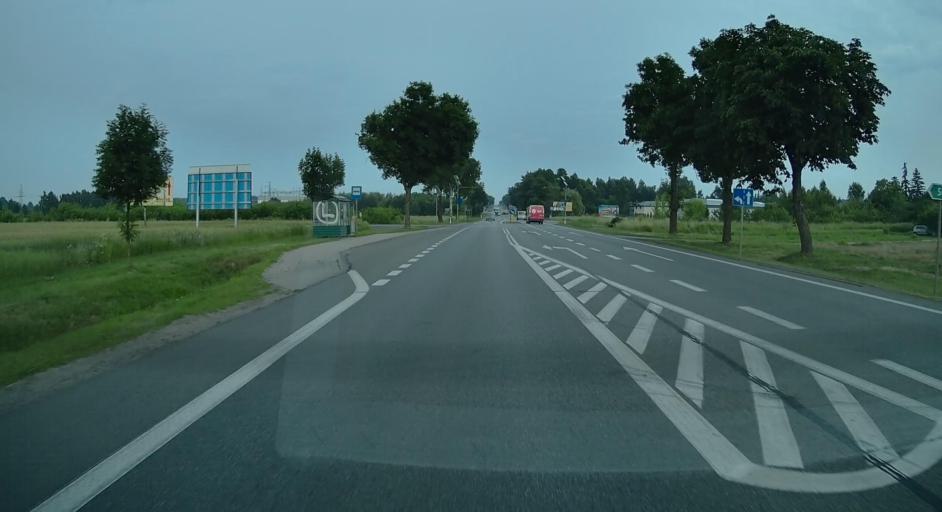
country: PL
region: Masovian Voivodeship
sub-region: Siedlce
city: Siedlce
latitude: 52.1307
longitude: 22.3327
